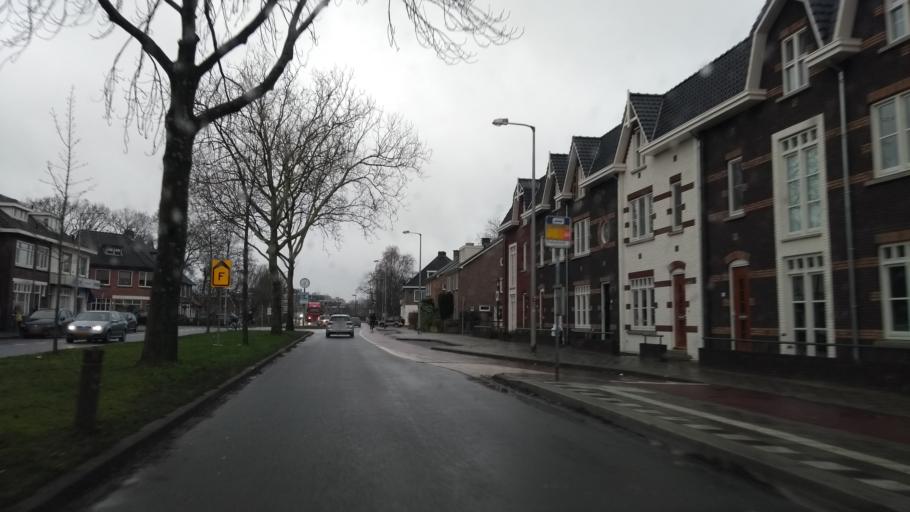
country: NL
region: Overijssel
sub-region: Gemeente Enschede
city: Enschede
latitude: 52.2264
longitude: 6.9093
